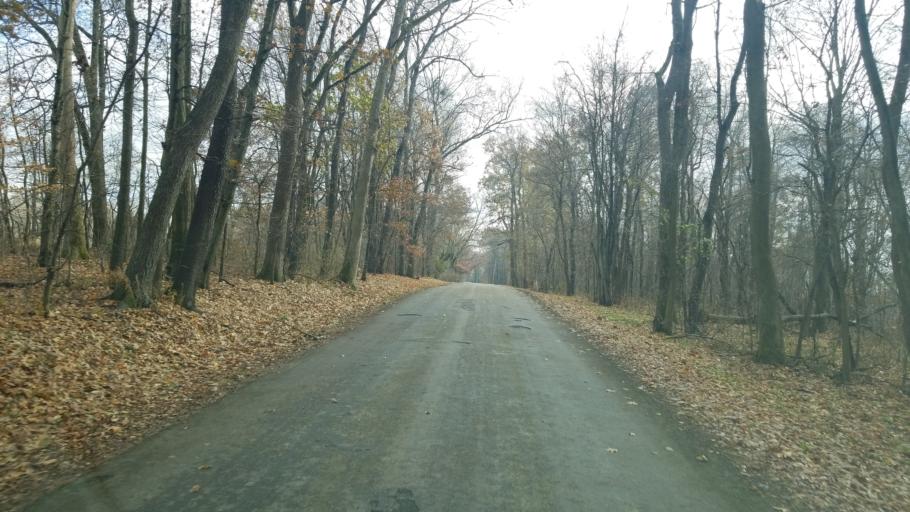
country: US
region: Ohio
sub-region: Richland County
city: Lincoln Heights
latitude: 40.8302
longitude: -82.4469
